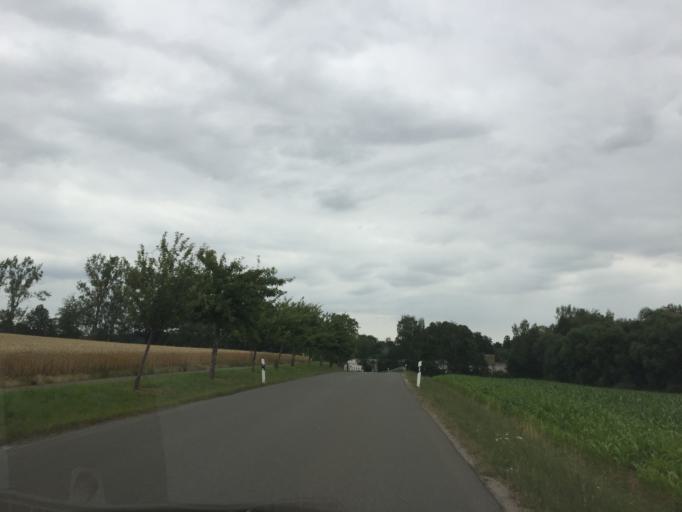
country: DE
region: Thuringia
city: Schmolln
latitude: 50.8837
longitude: 12.3353
